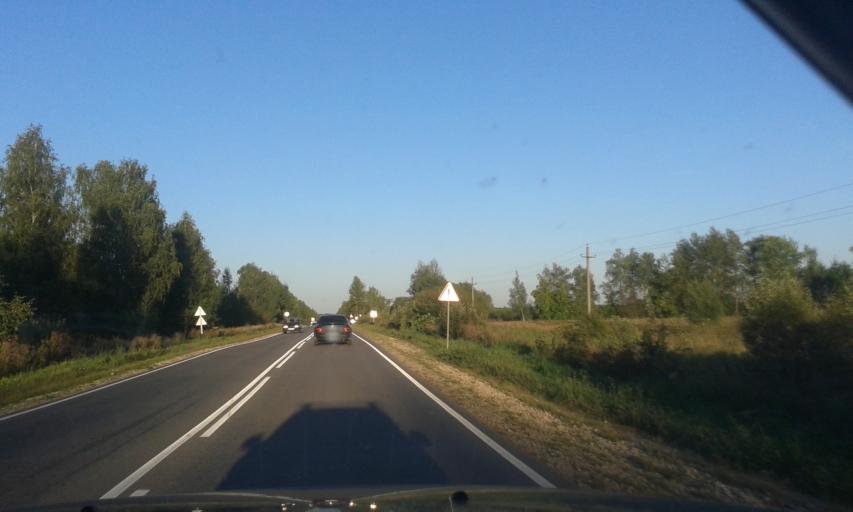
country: RU
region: Tula
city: Leninskiy
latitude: 54.1324
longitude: 37.2962
